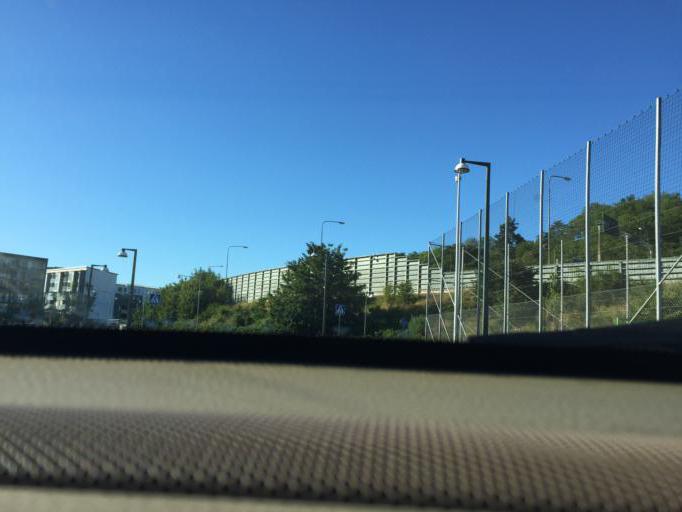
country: SE
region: Stockholm
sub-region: Stockholms Kommun
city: OEstermalm
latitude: 59.3078
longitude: 18.1072
